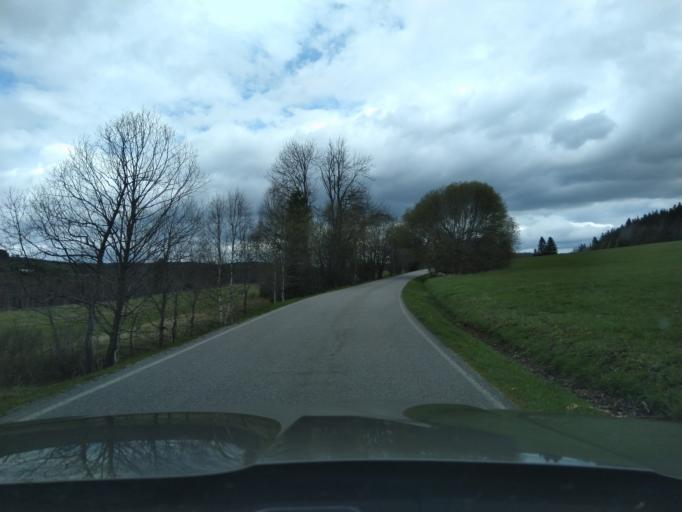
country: CZ
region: Jihocesky
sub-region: Okres Prachatice
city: Borova Lada
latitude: 49.0350
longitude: 13.6668
